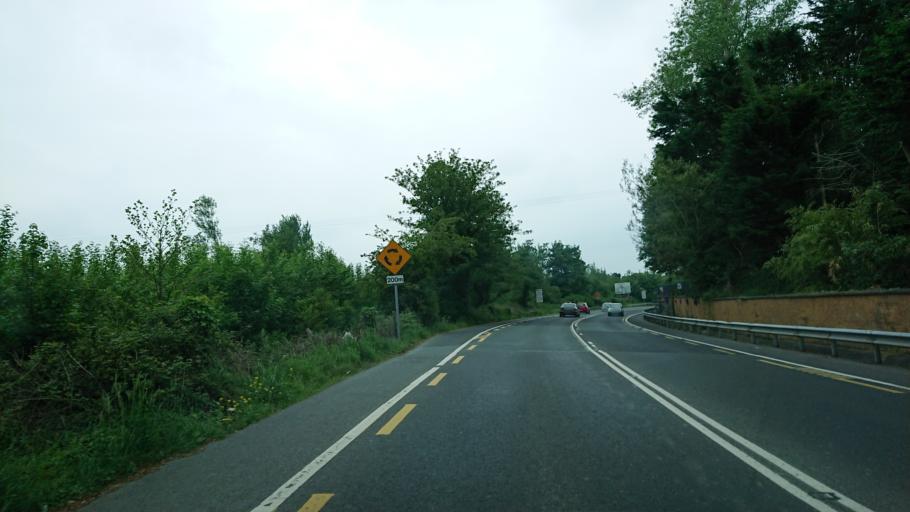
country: IE
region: Munster
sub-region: Waterford
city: Waterford
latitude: 52.2220
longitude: -7.1279
